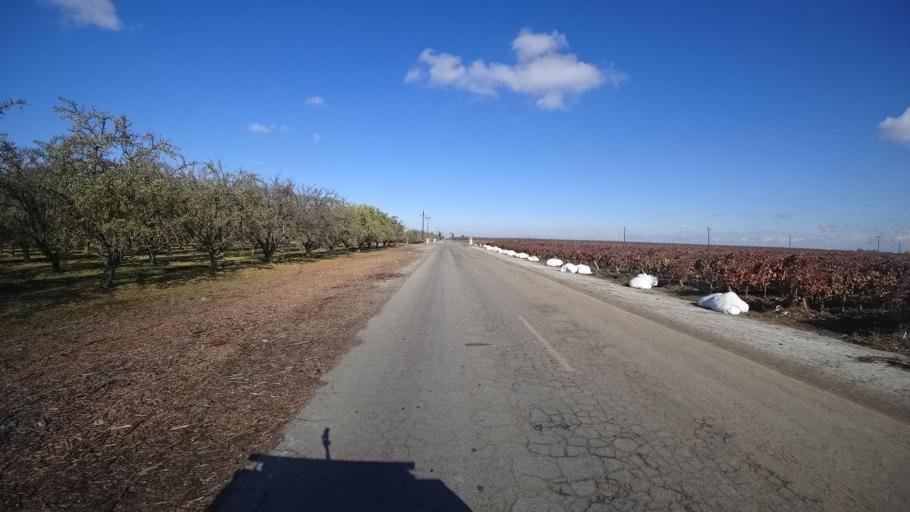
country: US
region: California
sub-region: Kern County
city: McFarland
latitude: 35.6879
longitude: -119.2587
